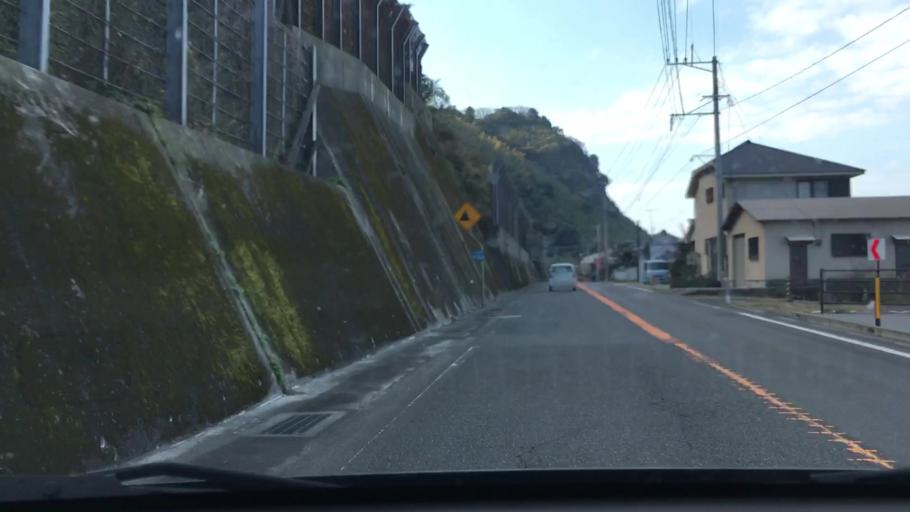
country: JP
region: Kagoshima
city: Hamanoichi
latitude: 31.6071
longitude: 130.7923
